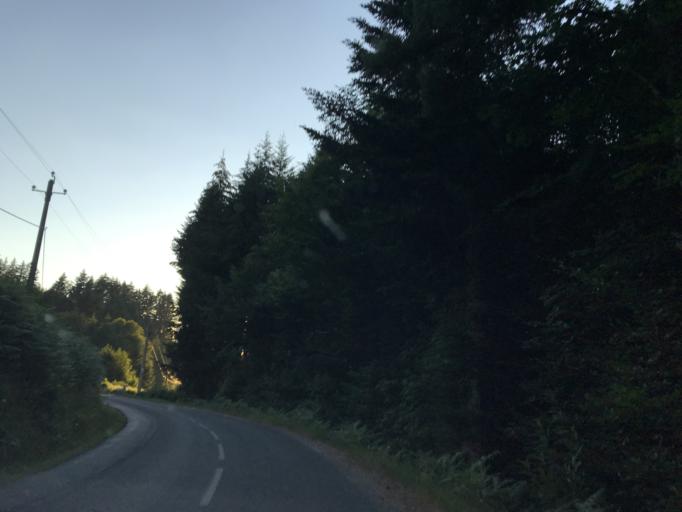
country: FR
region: Auvergne
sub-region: Departement du Puy-de-Dome
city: Chabreloche
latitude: 45.8275
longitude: 3.6959
